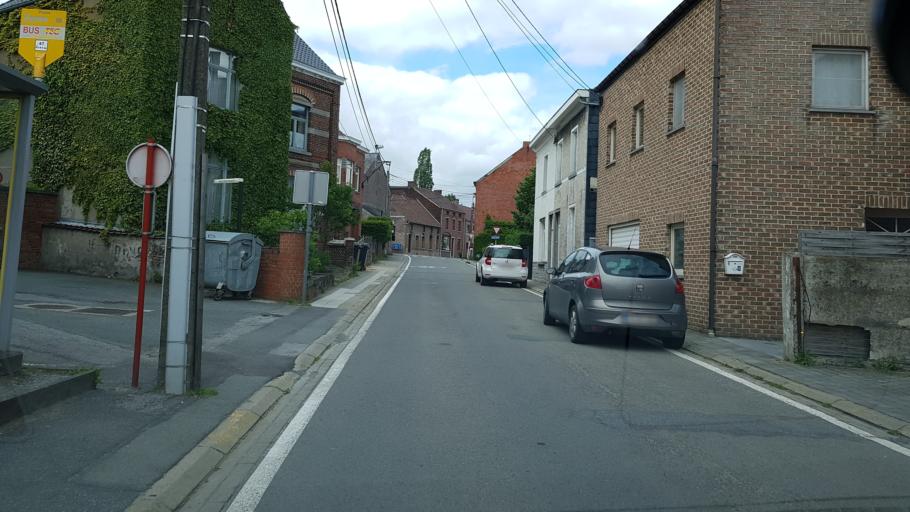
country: BE
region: Wallonia
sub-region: Province du Brabant Wallon
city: Tubize
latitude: 50.6405
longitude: 4.2059
